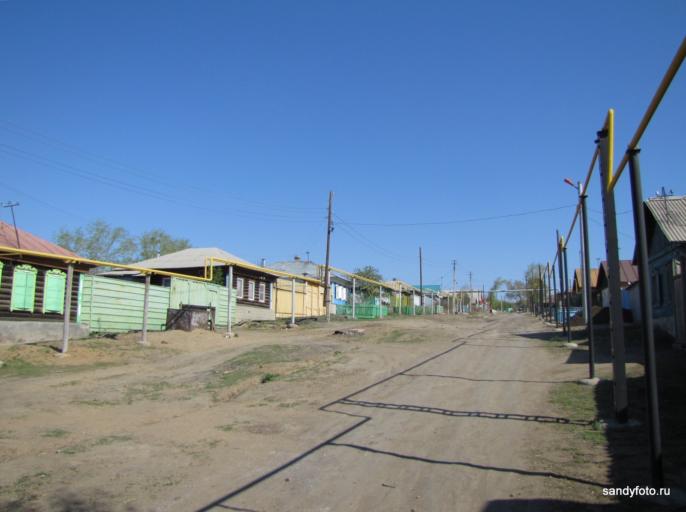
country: RU
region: Chelyabinsk
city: Troitsk
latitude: 54.0989
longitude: 61.5612
